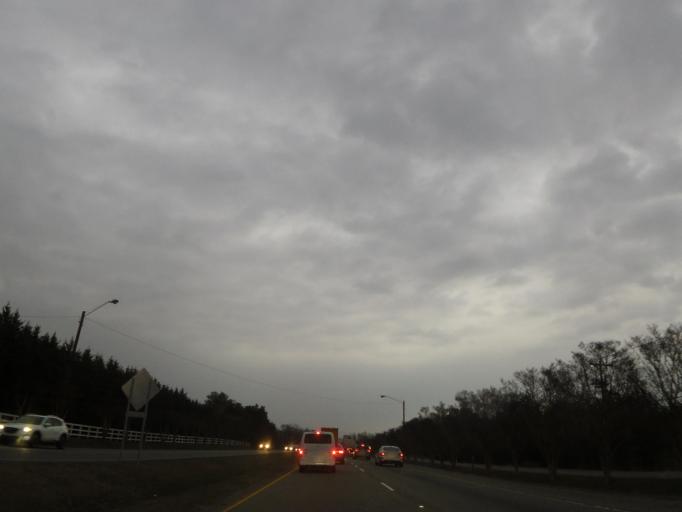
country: US
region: South Carolina
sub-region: Greenville County
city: Travelers Rest
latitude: 34.9777
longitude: -82.4279
